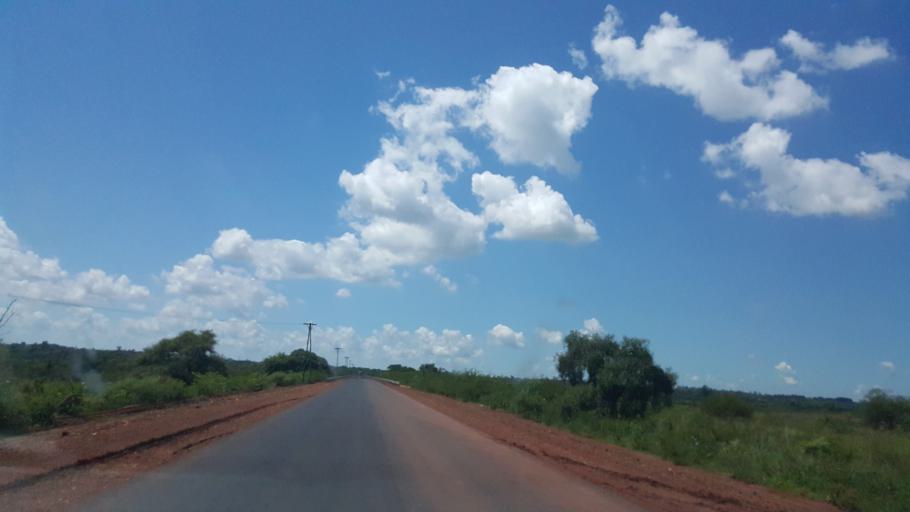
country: AR
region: Corrientes
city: Santo Tome
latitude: -28.5273
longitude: -56.0545
